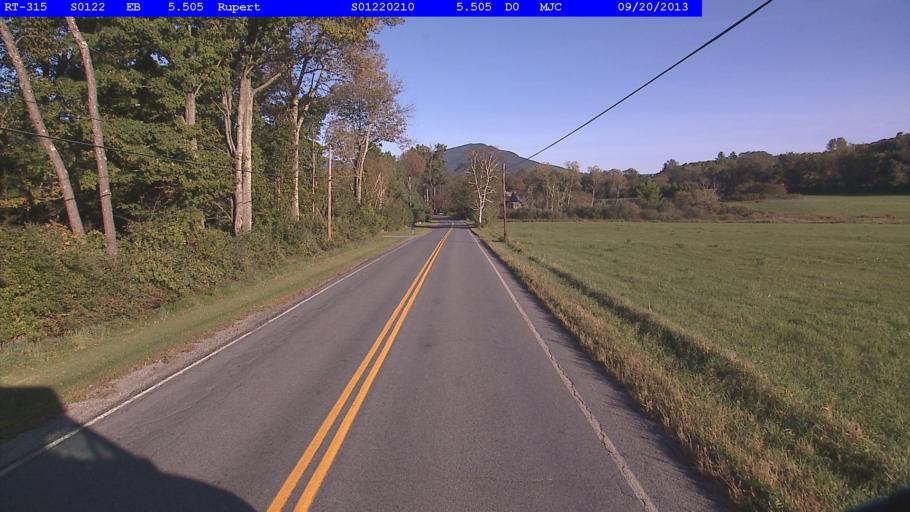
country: US
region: Vermont
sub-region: Bennington County
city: Manchester Center
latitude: 43.2741
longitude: -73.1308
